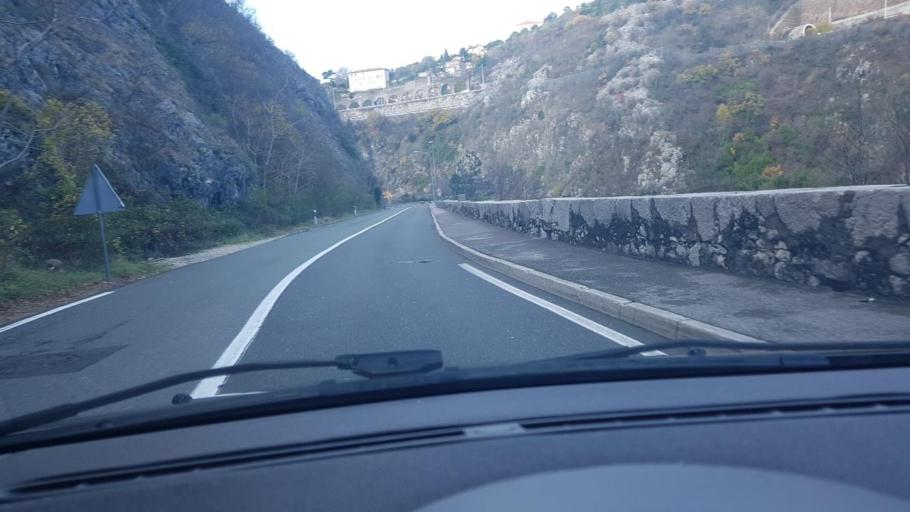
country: HR
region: Primorsko-Goranska
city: Drenova
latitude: 45.3333
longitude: 14.4559
